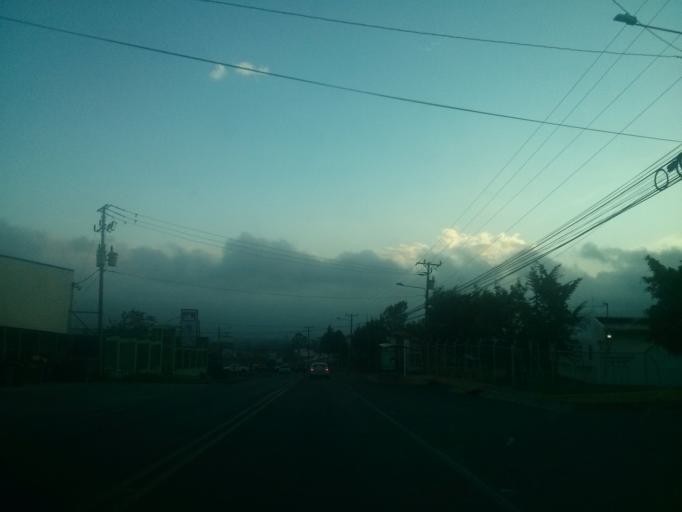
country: CR
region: Cartago
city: Cartago
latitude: 9.8791
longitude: -83.9235
